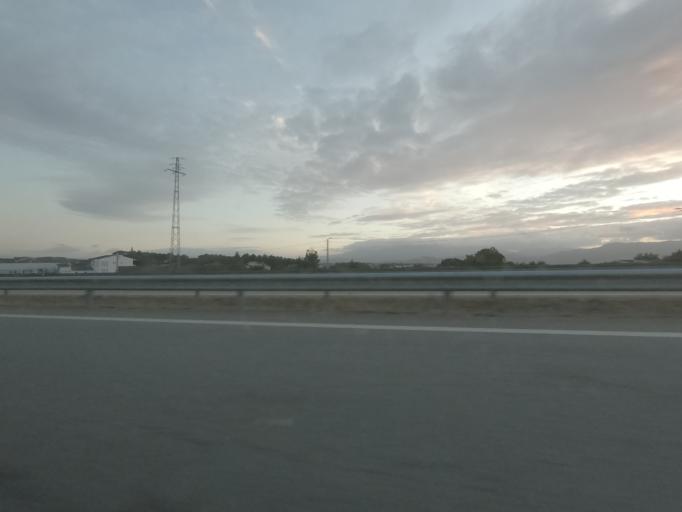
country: PT
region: Vila Real
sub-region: Vila Real
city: Vila Real
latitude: 41.2803
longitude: -7.6909
